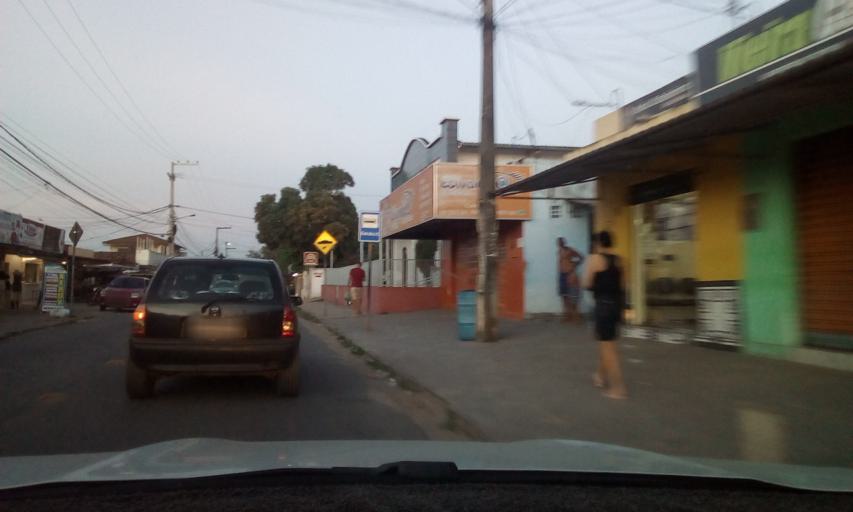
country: BR
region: Paraiba
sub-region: Bayeux
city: Bayeux
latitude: -7.1695
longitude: -34.9114
